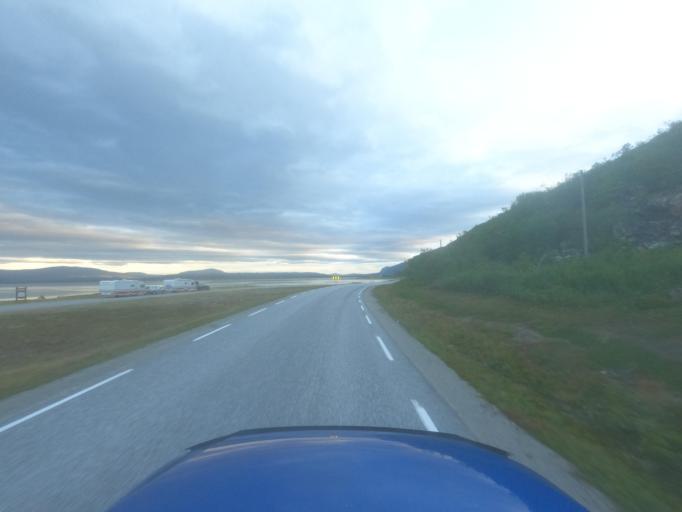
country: NO
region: Finnmark Fylke
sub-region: Porsanger
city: Lakselv
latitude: 70.1126
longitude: 24.9186
